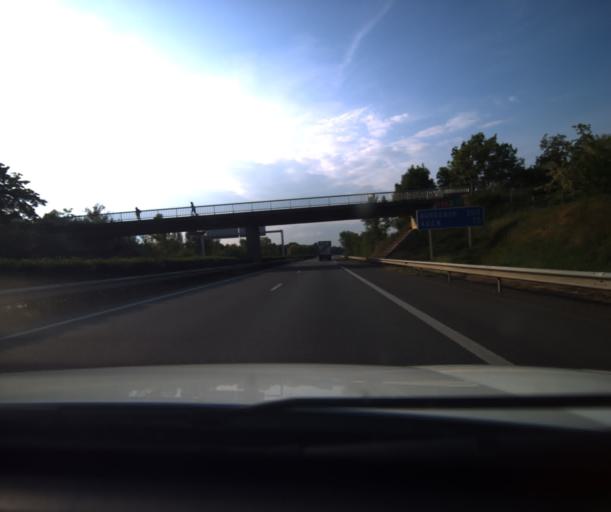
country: FR
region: Midi-Pyrenees
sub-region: Departement du Tarn-et-Garonne
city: Campsas
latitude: 43.9370
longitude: 1.2992
